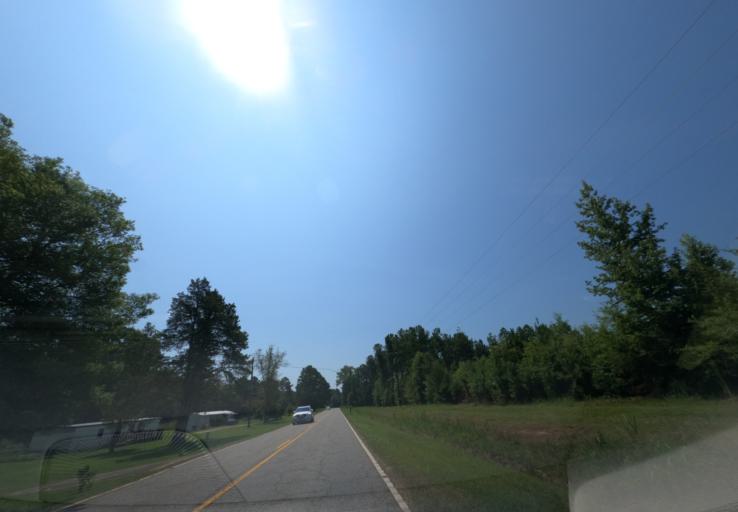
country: US
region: South Carolina
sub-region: Greenwood County
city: Greenwood
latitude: 34.0460
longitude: -82.1340
